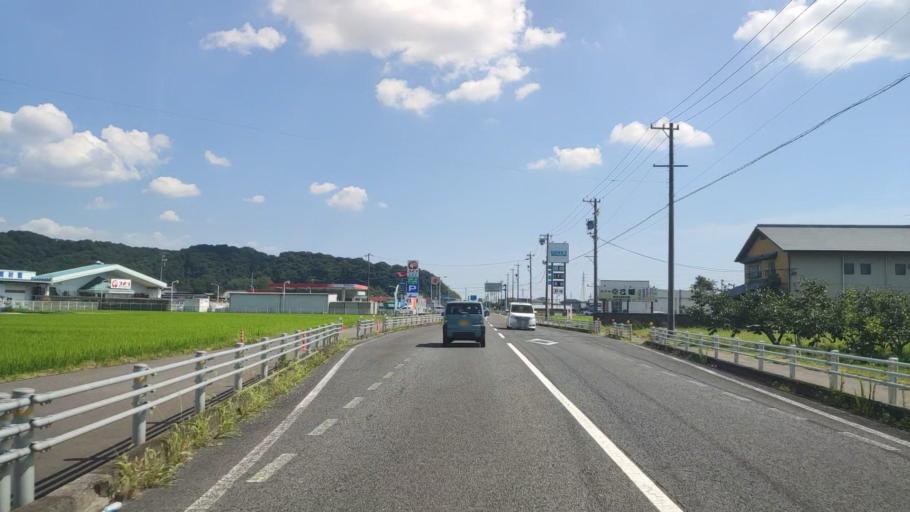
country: JP
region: Gifu
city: Godo
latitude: 35.4826
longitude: 136.6742
